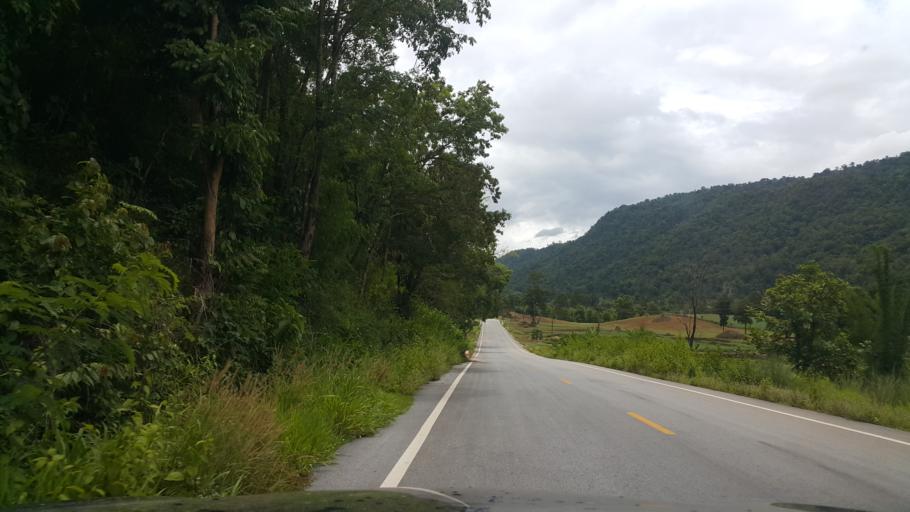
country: TH
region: Phitsanulok
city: Chat Trakan
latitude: 17.3550
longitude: 100.7297
